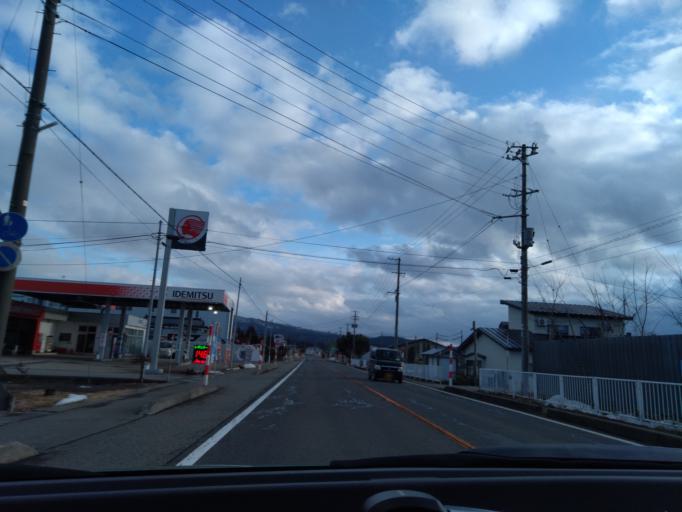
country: JP
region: Akita
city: Yokotemachi
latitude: 39.4037
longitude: 140.5603
